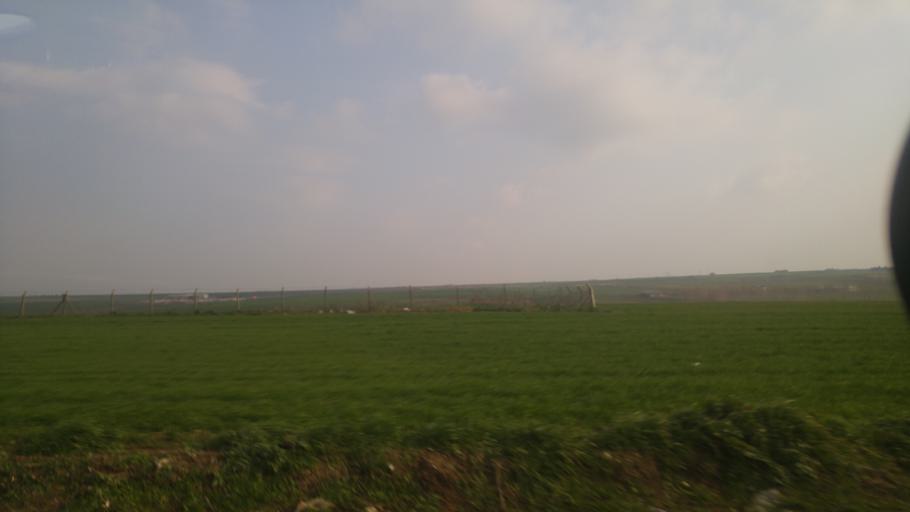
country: TR
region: Istanbul
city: Silivri
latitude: 41.0950
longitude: 28.2774
